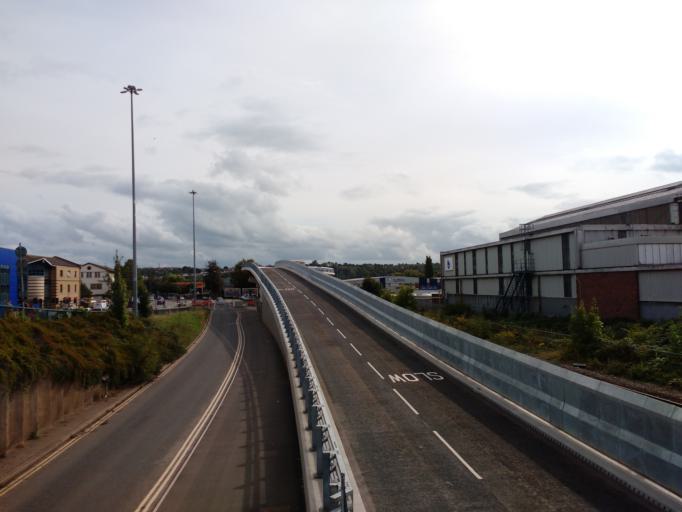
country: GB
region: England
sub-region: Bristol
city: Bristol
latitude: 51.4406
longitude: -2.6248
